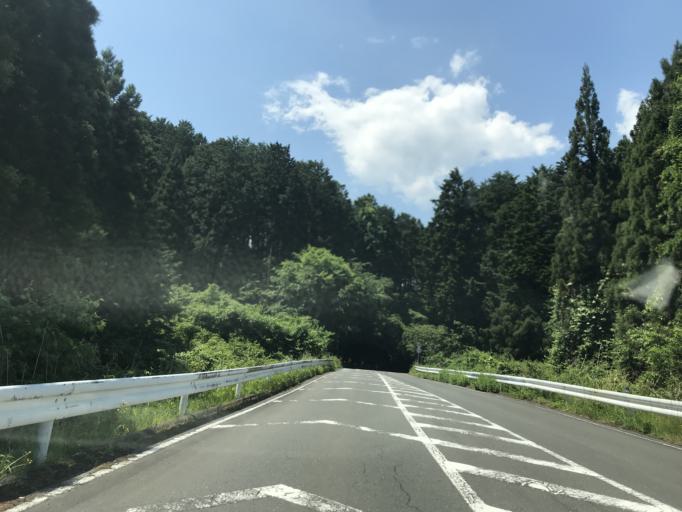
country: JP
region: Miyagi
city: Matsushima
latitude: 38.3674
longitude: 141.0511
